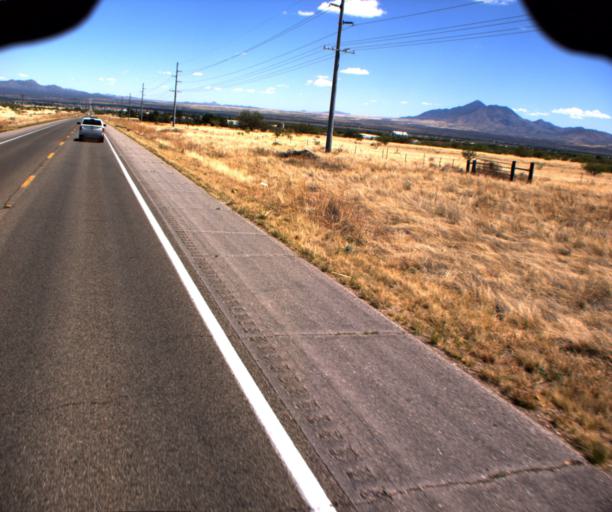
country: US
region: Arizona
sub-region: Cochise County
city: Sierra Vista Southeast
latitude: 31.3799
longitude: -110.1969
